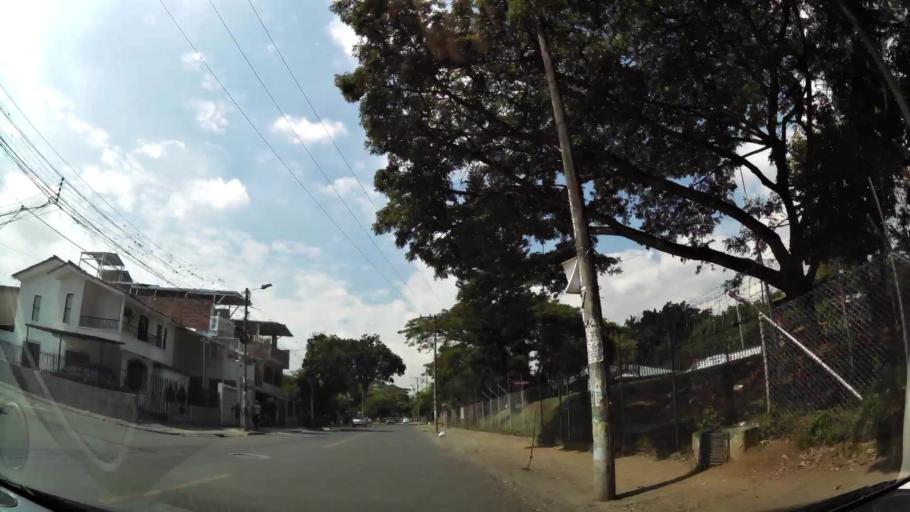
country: CO
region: Valle del Cauca
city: Cali
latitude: 3.4901
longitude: -76.5012
